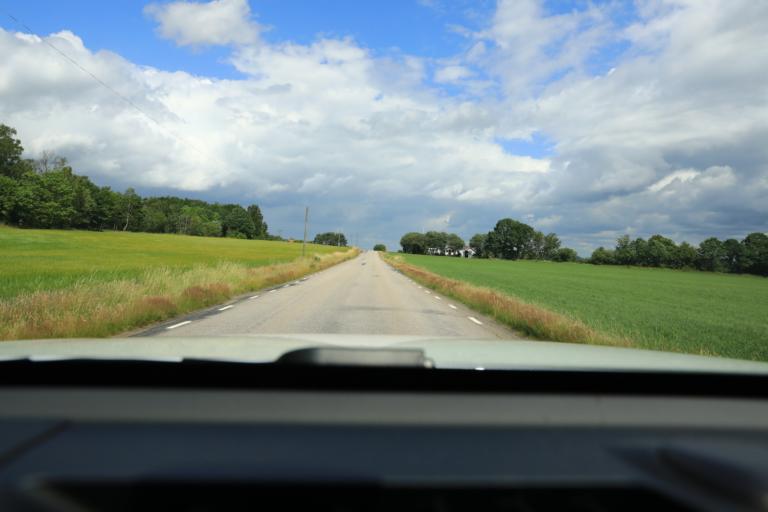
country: SE
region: Halland
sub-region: Varbergs Kommun
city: Tvaaker
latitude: 57.0892
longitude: 12.4076
